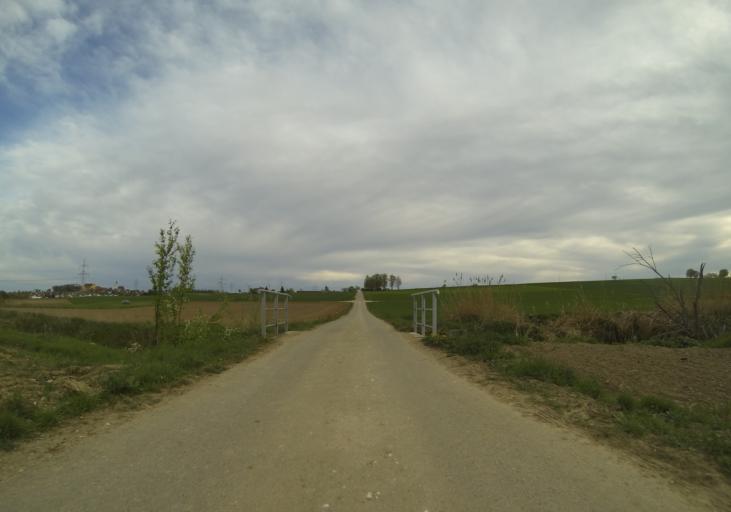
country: DE
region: Baden-Wuerttemberg
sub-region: Tuebingen Region
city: Erbach
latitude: 48.3302
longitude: 9.8699
